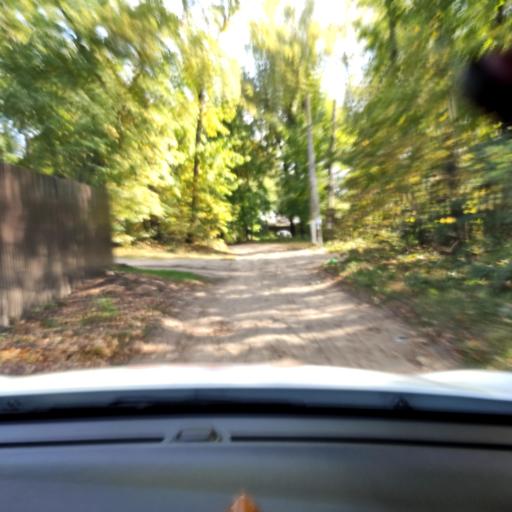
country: RU
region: Tatarstan
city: Staroye Arakchino
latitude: 55.8075
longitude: 49.0135
